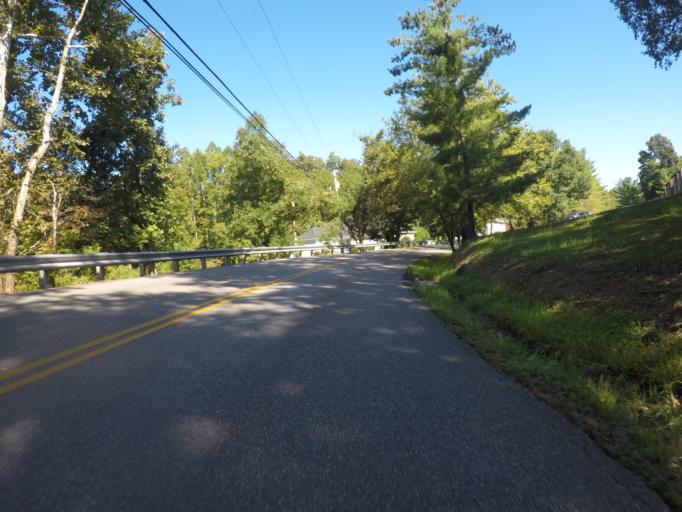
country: US
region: Kentucky
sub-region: Greenup County
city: Russell
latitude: 38.5066
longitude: -82.6960
